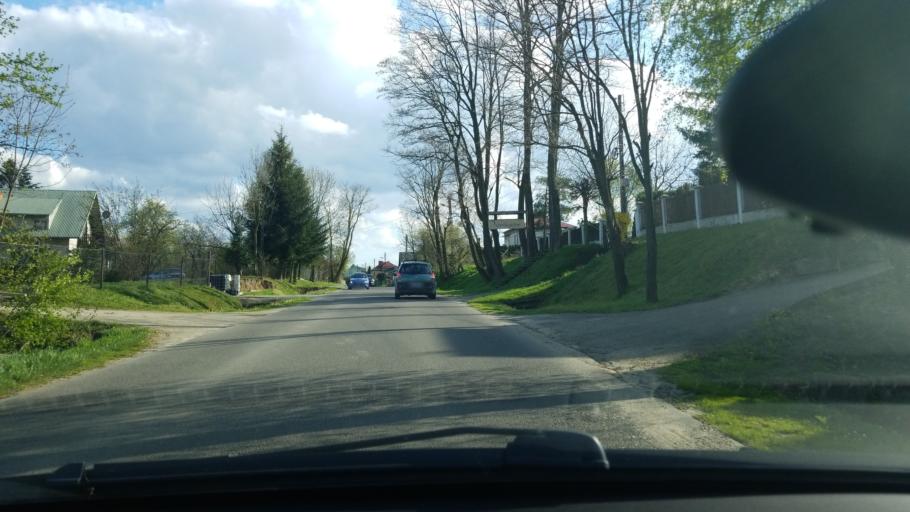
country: PL
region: Subcarpathian Voivodeship
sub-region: Powiat jasielski
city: Debowiec
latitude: 49.6881
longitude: 21.4618
